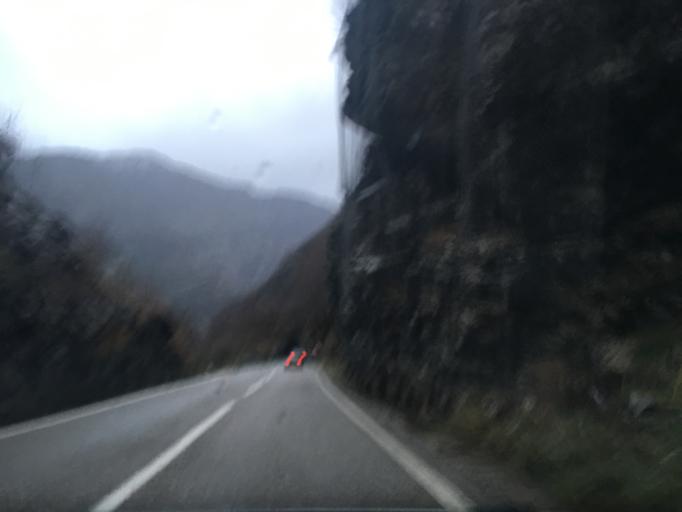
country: ME
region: Opstina Kolasin
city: Kolasin
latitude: 42.6632
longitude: 19.3718
